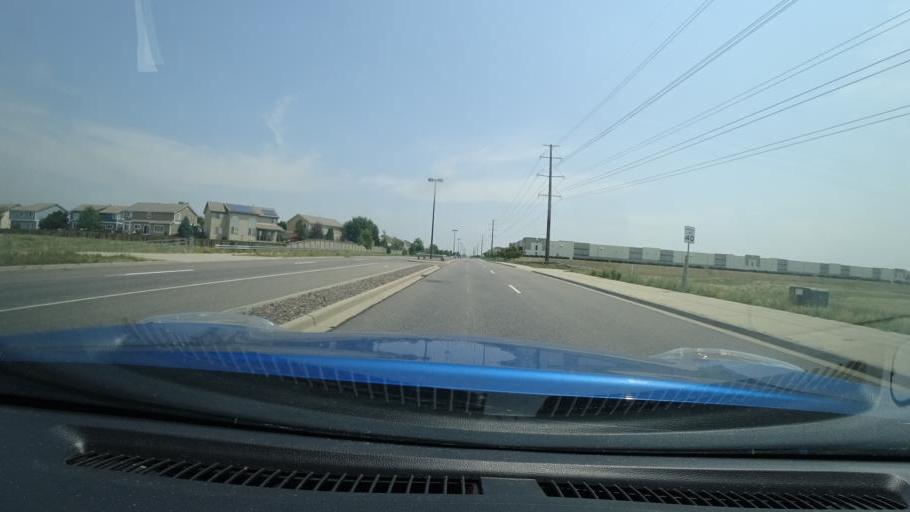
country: US
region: Colorado
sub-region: Adams County
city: Aurora
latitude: 39.7691
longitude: -104.7653
